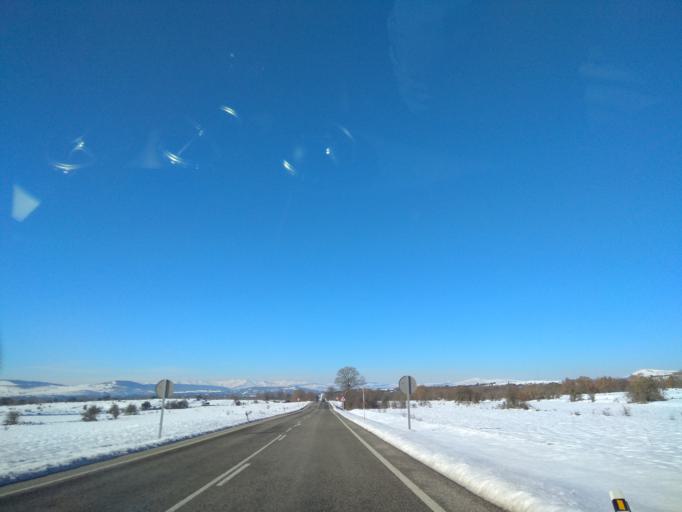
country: ES
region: Cantabria
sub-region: Provincia de Cantabria
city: San Martin de Elines
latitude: 42.9367
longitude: -3.7250
